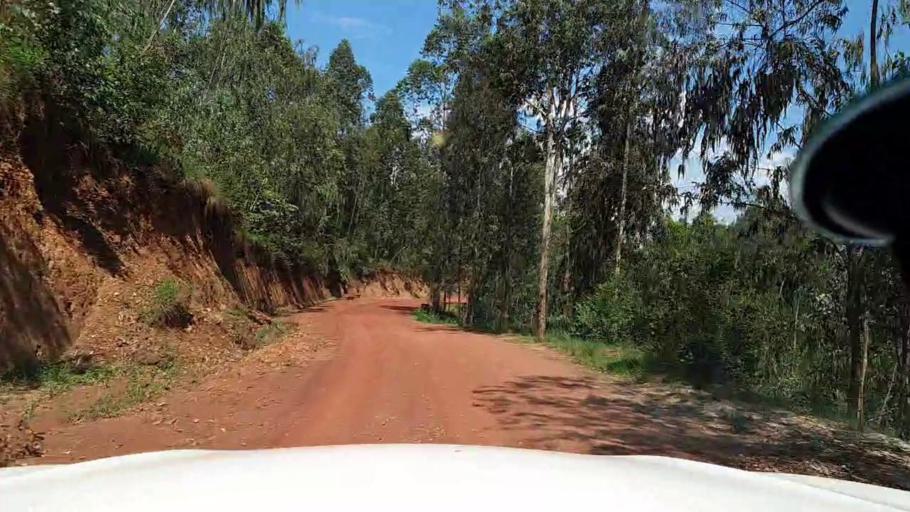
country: RW
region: Kigali
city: Kigali
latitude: -1.7652
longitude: 29.8734
